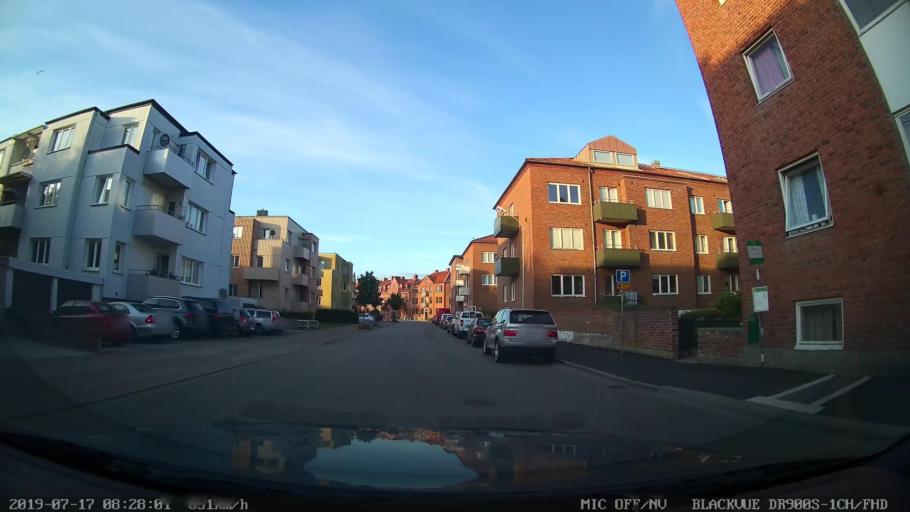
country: SE
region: Skane
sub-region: Landskrona
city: Landskrona
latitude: 55.8729
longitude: 12.8413
